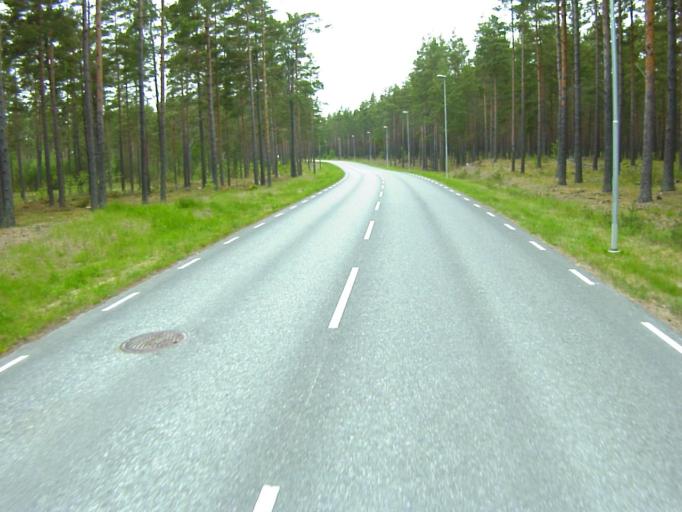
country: SE
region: Skane
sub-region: Kristianstads Kommun
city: Ahus
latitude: 55.9482
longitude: 14.2974
